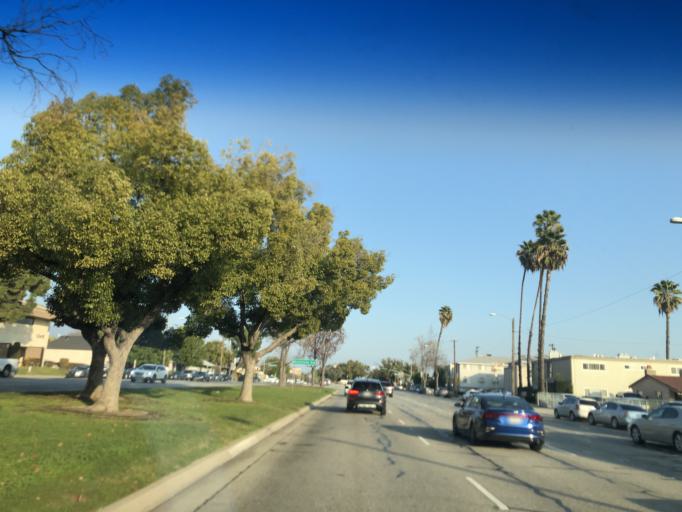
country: US
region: California
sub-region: Los Angeles County
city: Temple City
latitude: 34.1306
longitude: -118.0697
